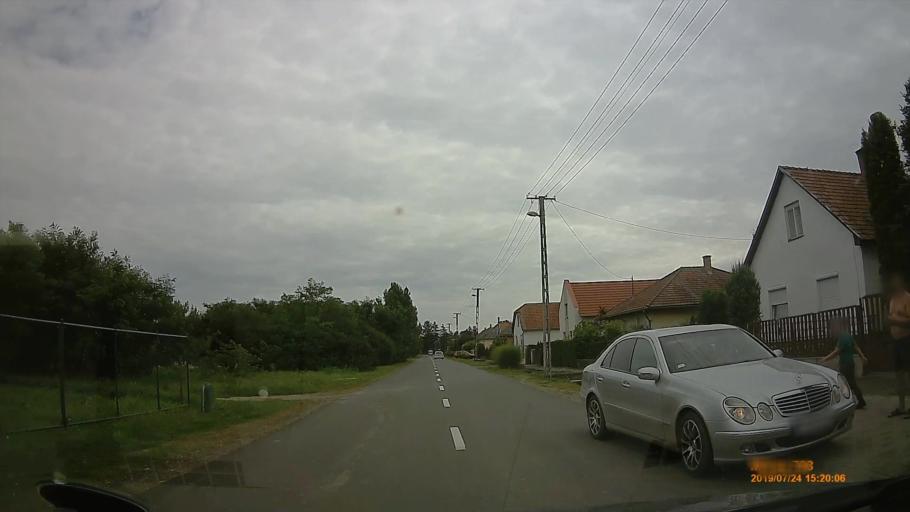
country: HU
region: Szabolcs-Szatmar-Bereg
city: Tarpa
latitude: 48.1650
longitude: 22.5446
